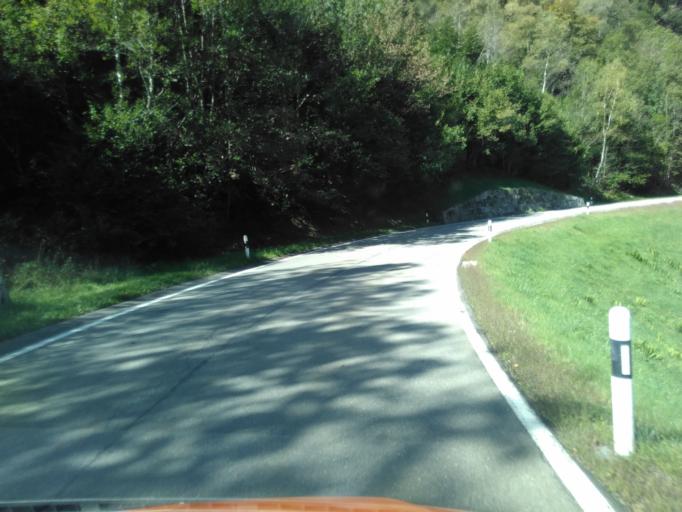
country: CH
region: Grisons
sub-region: Moesa District
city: Cauco
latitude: 46.3286
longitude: 9.1177
